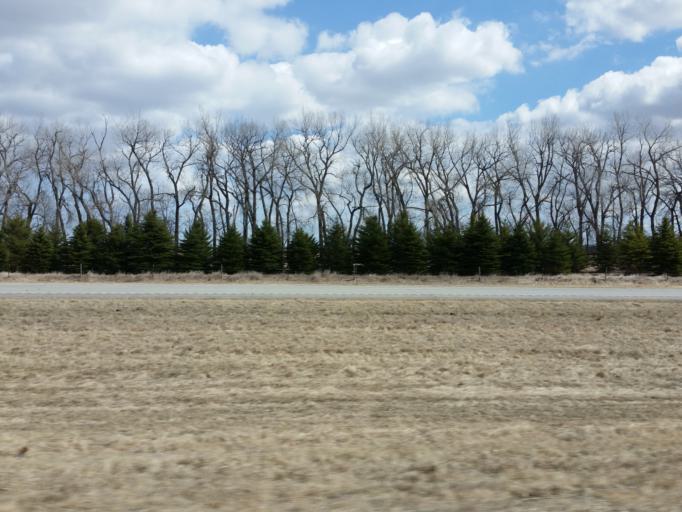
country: US
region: South Dakota
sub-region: Codington County
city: Watertown
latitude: 45.1240
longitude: -97.0565
